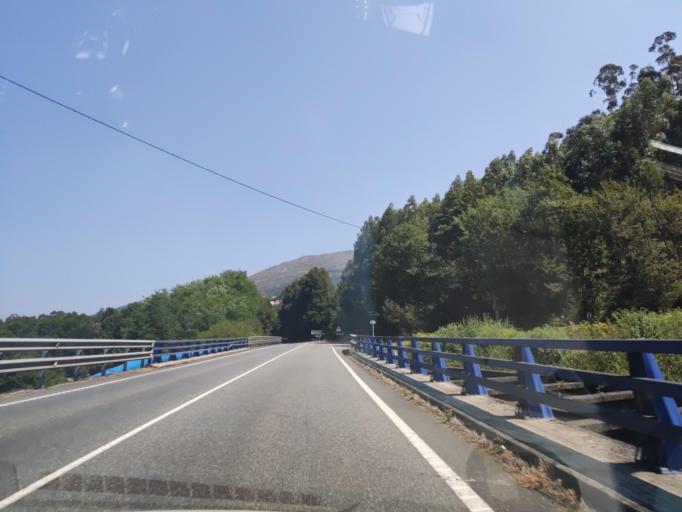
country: ES
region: Galicia
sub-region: Provincia de Pontevedra
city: Porrino
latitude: 42.2161
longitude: -8.5979
